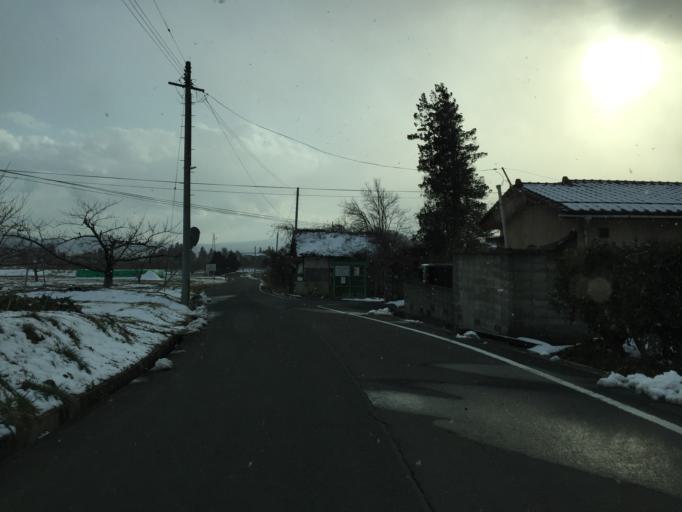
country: JP
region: Fukushima
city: Fukushima-shi
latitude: 37.8396
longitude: 140.4622
